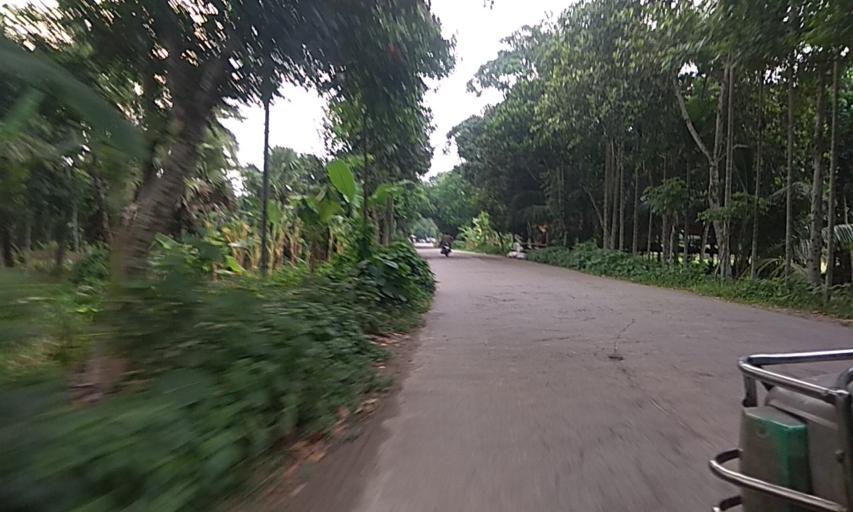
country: BD
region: Dhaka
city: Dohar
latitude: 23.4607
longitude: 89.9974
